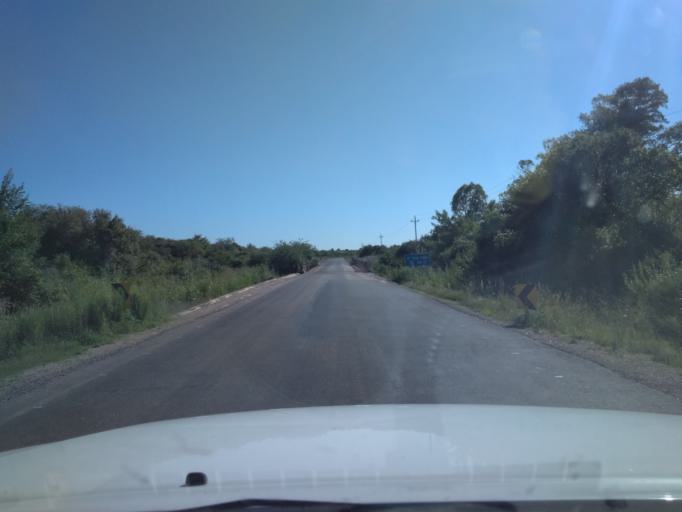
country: UY
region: Canelones
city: San Ramon
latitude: -34.2710
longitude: -55.9428
